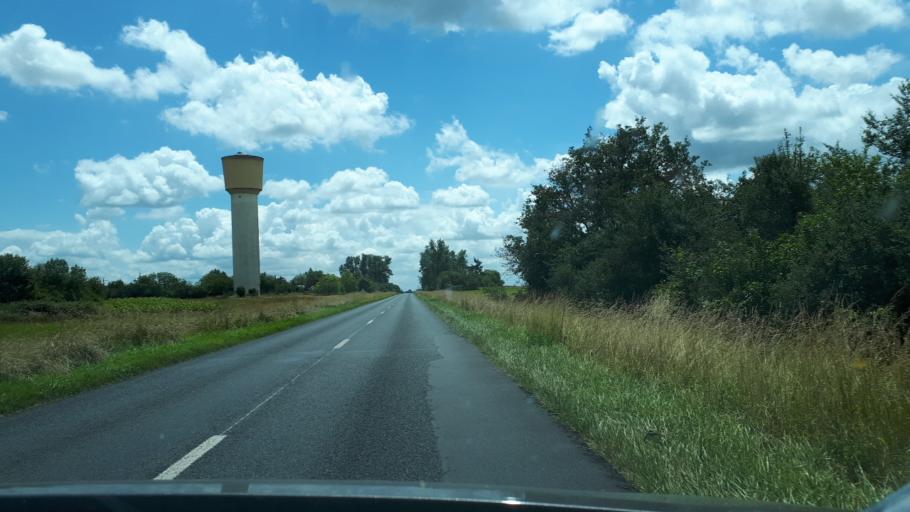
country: FR
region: Centre
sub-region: Departement du Loir-et-Cher
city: Contres
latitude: 47.3900
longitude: 1.4084
